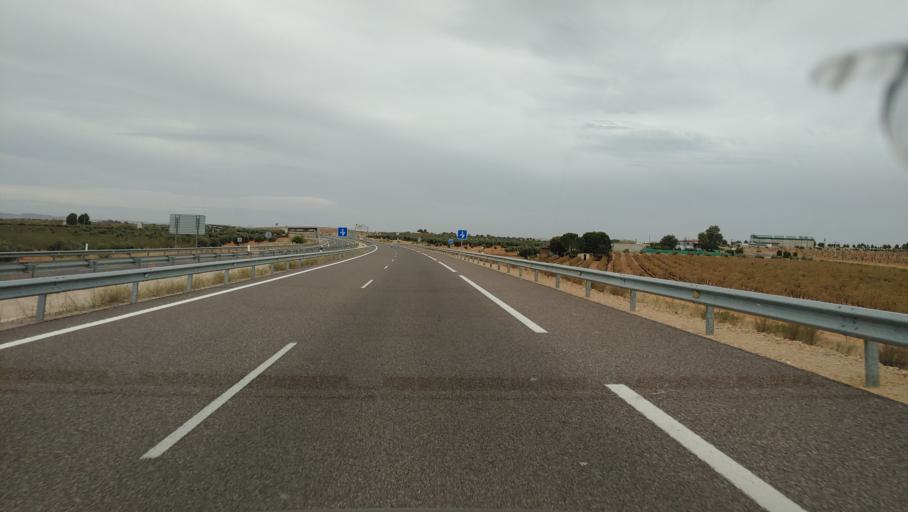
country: ES
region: Castille-La Mancha
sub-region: Provincia de Ciudad Real
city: Valenzuela de Calatrava
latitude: 38.9023
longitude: -3.8053
